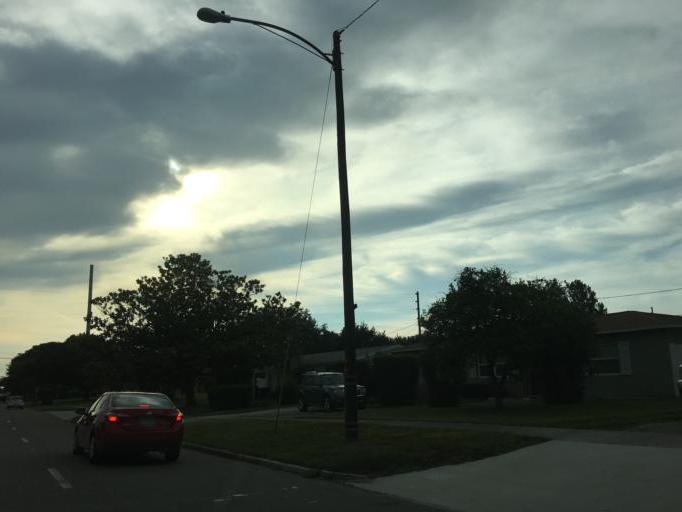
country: US
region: Florida
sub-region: Pinellas County
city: Kenneth City
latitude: 27.7918
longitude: -82.7055
